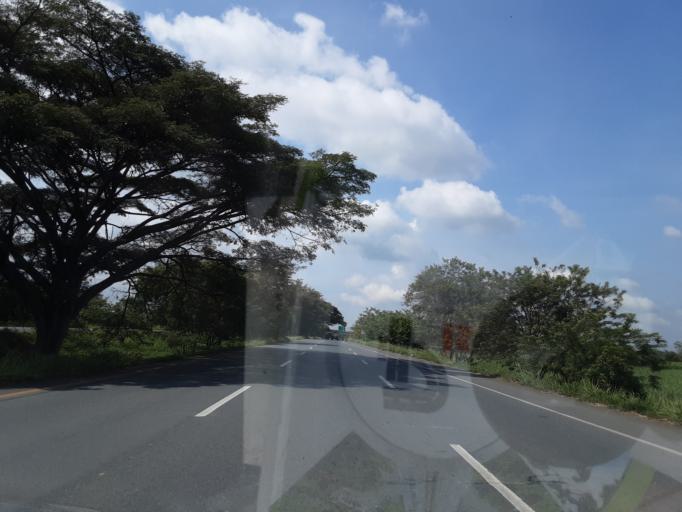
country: CO
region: Valle del Cauca
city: El Cerrito
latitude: 3.7235
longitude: -76.3208
